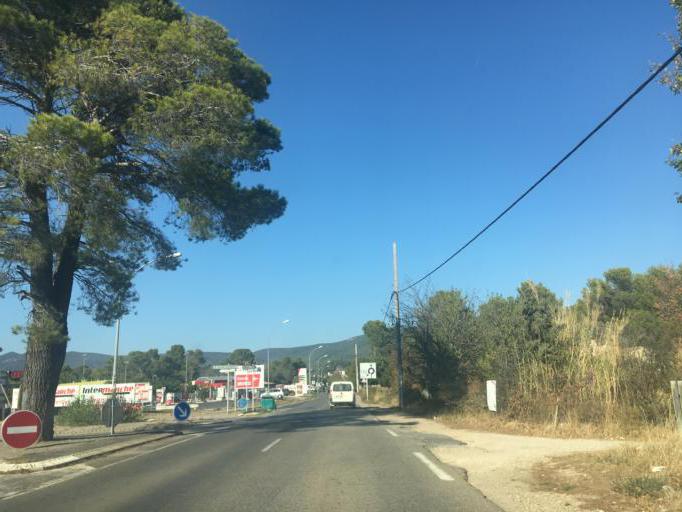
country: FR
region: Provence-Alpes-Cote d'Azur
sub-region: Departement du Var
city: Aups
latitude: 43.6151
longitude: 6.2194
